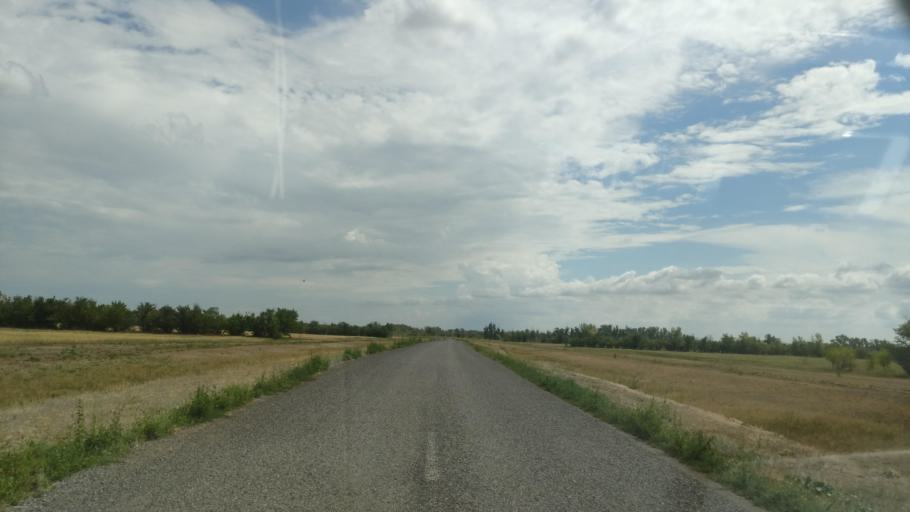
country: KZ
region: Pavlodar
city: Pavlodar
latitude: 52.6367
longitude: 76.9822
